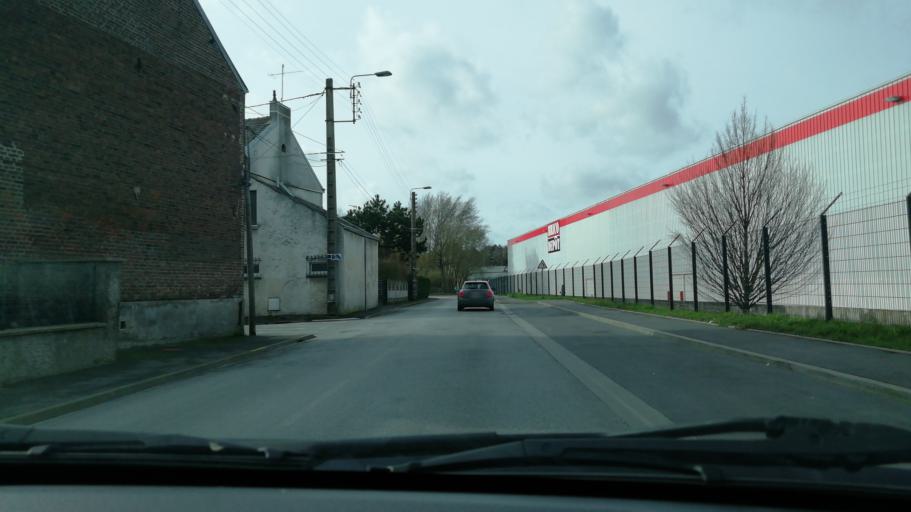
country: FR
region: Nord-Pas-de-Calais
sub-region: Departement du Nord
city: Maubeuge
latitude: 50.2805
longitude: 3.9556
